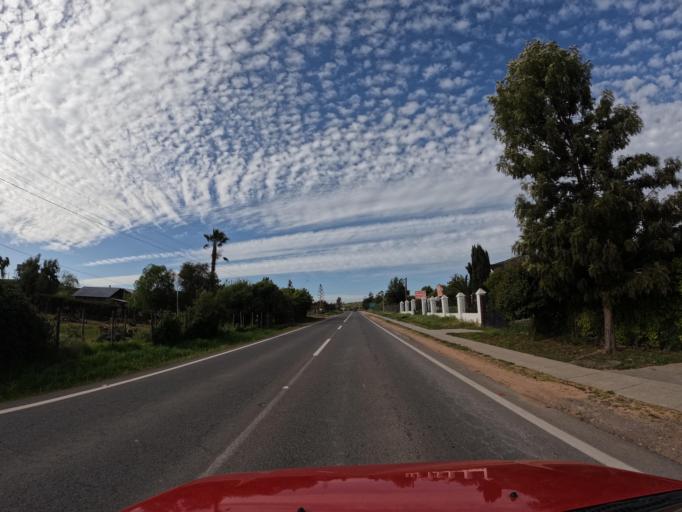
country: CL
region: O'Higgins
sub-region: Provincia de Colchagua
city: Santa Cruz
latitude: -34.2586
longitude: -71.7290
